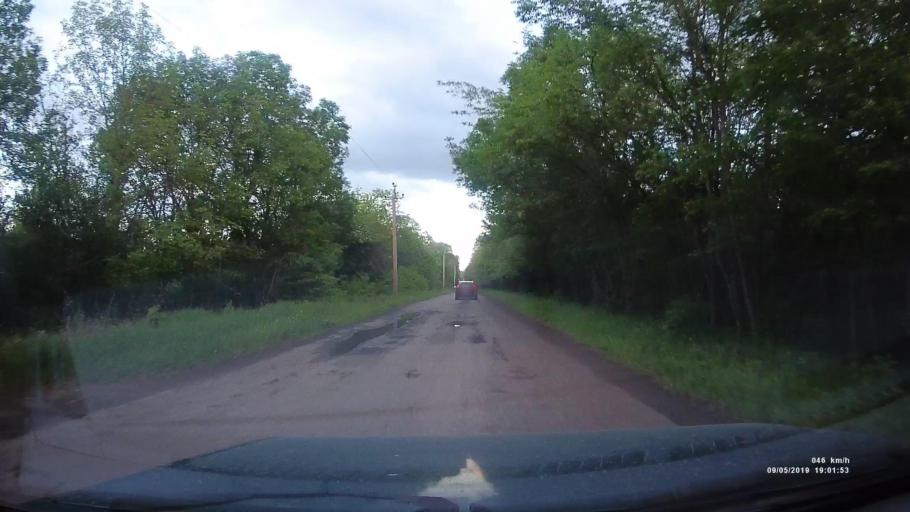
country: RU
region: Krasnodarskiy
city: Kanelovskaya
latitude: 46.7468
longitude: 39.1475
